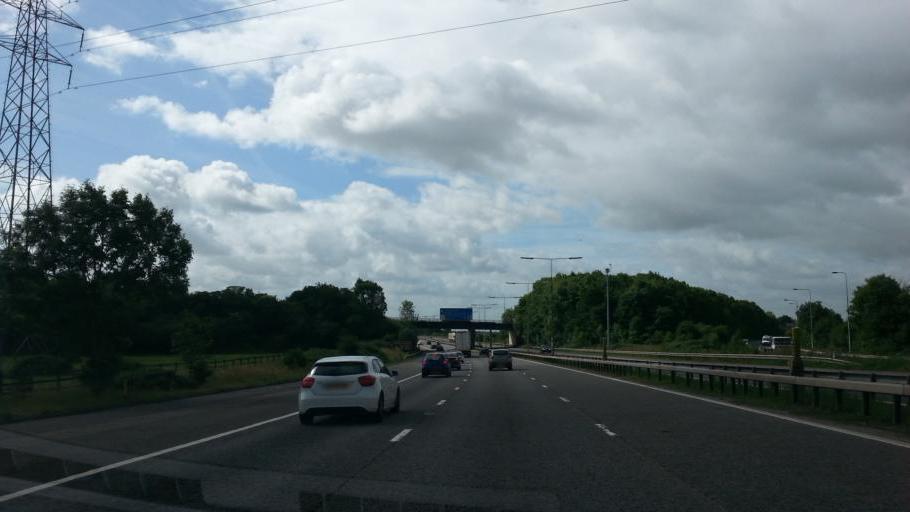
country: GB
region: England
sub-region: Warwickshire
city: Bedworth
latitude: 52.4439
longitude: -1.4254
